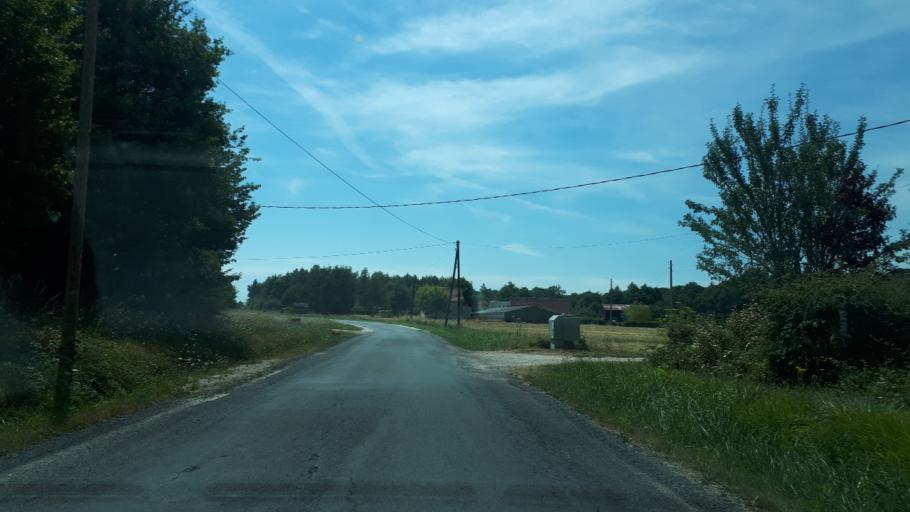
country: FR
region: Centre
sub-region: Departement du Loir-et-Cher
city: Contres
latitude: 47.4196
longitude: 1.3558
